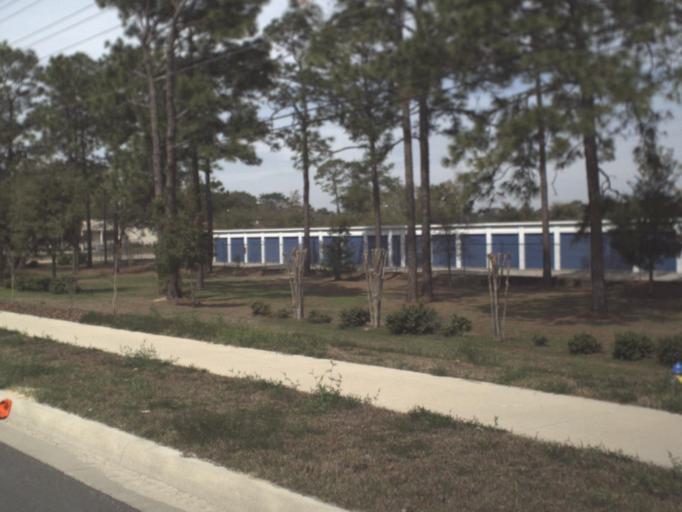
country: US
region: Florida
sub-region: Leon County
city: Tallahassee
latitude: 30.3759
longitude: -84.2782
